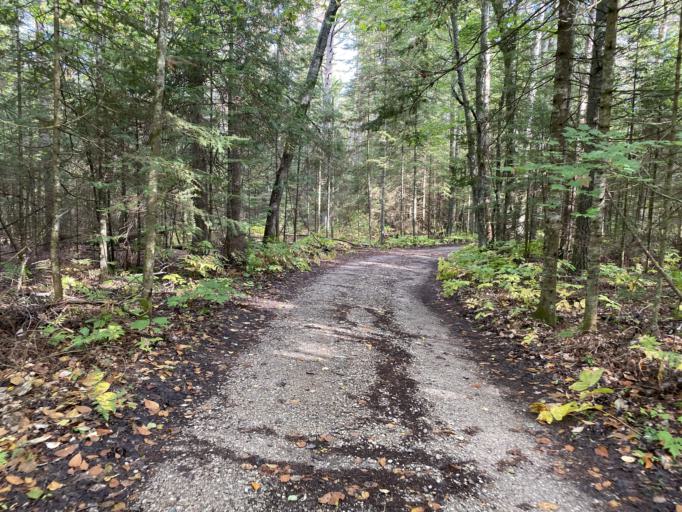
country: US
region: Michigan
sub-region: Mackinac County
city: Saint Ignace
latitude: 45.7487
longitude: -84.8795
